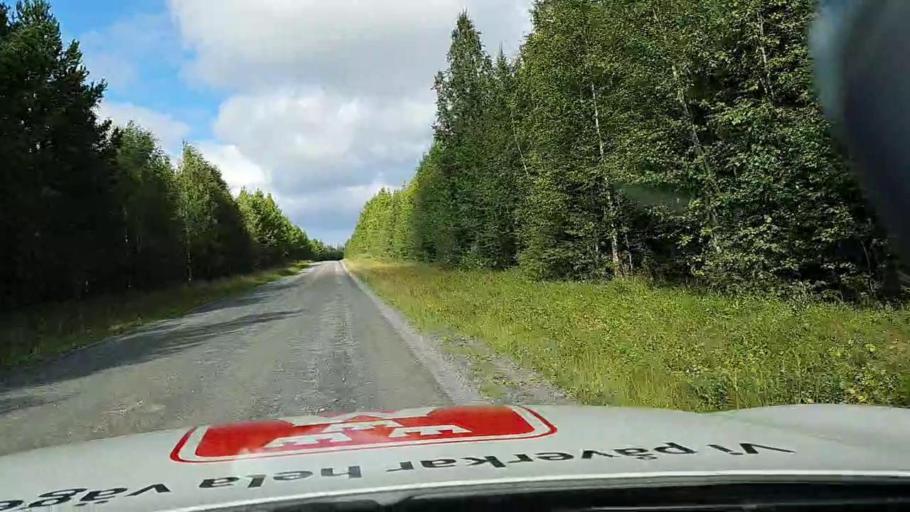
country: SE
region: Jaemtland
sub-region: Stroemsunds Kommun
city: Stroemsund
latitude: 63.7485
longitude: 15.2346
